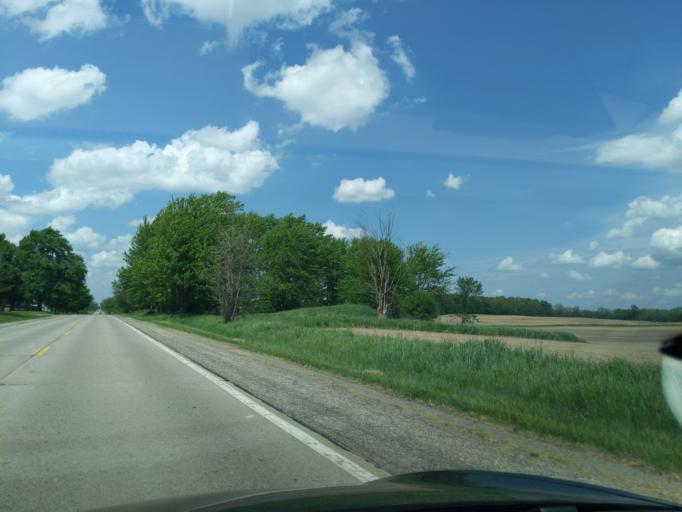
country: US
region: Michigan
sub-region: Ingham County
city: Okemos
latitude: 42.6565
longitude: -84.4329
